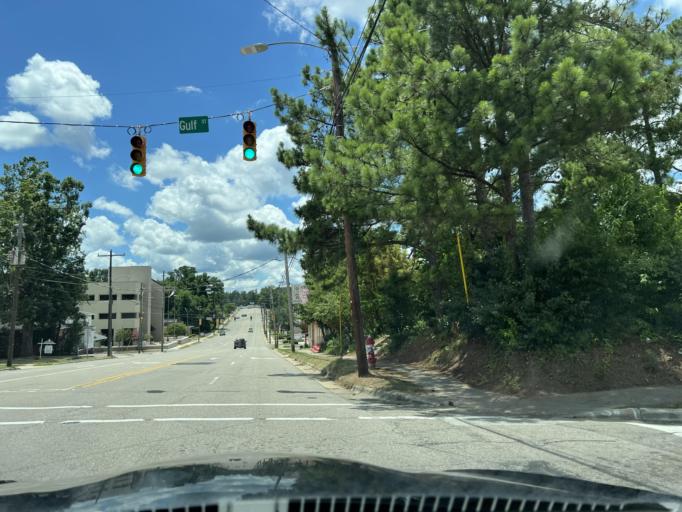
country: US
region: North Carolina
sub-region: Lee County
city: Sanford
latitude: 35.4792
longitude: -79.1821
